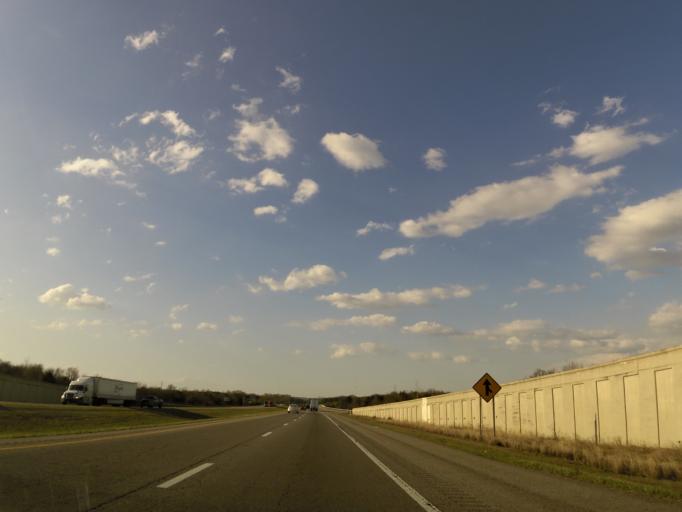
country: US
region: Tennessee
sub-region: Wilson County
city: Rural Hill
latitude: 36.0416
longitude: -86.4292
